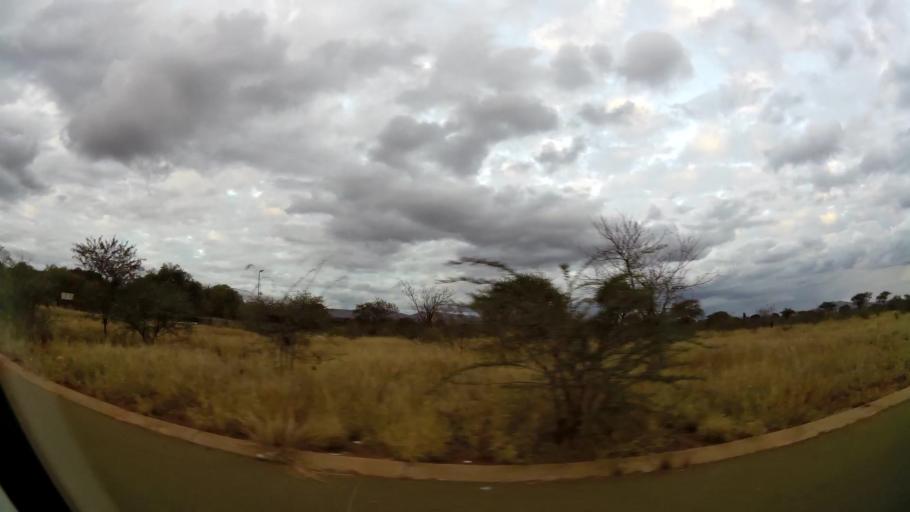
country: ZA
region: Limpopo
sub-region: Waterberg District Municipality
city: Mokopane
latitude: -24.1932
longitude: 29.0010
